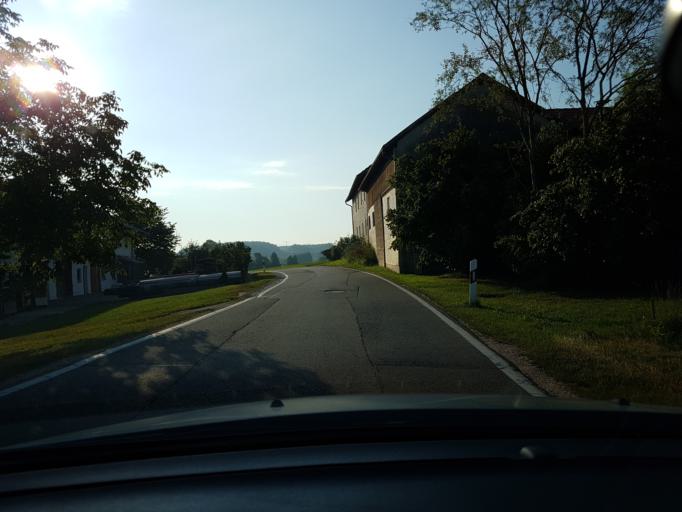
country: DE
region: Bavaria
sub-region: Upper Bavaria
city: Egglkofen
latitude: 48.4165
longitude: 12.4849
